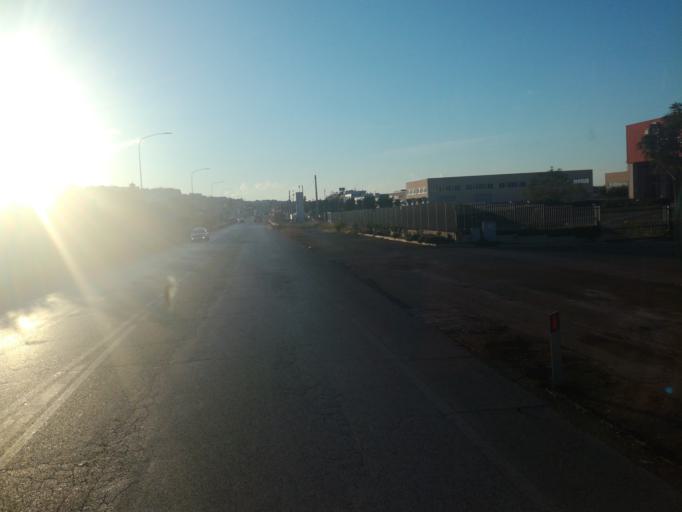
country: IT
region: Apulia
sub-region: Provincia di Taranto
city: Massafra
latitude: 40.5883
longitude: 17.1031
